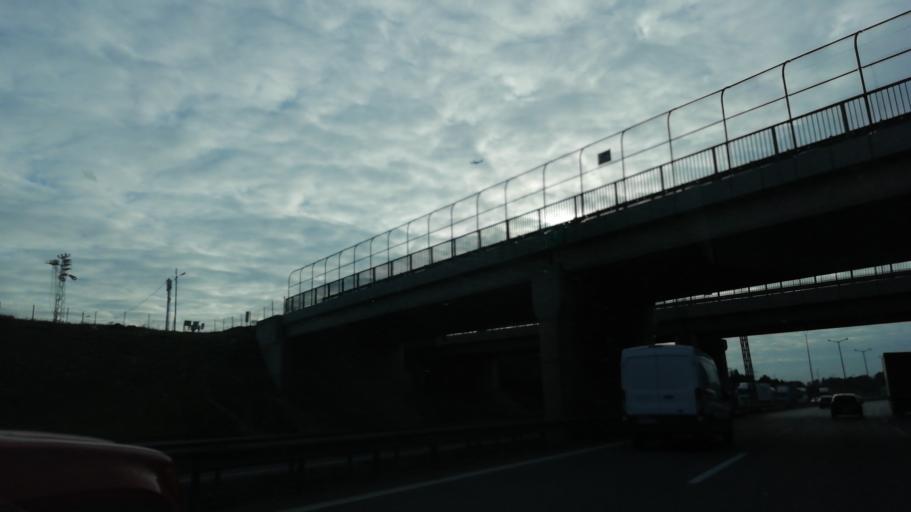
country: TR
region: Istanbul
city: Sultanbeyli
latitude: 40.9270
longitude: 29.3490
